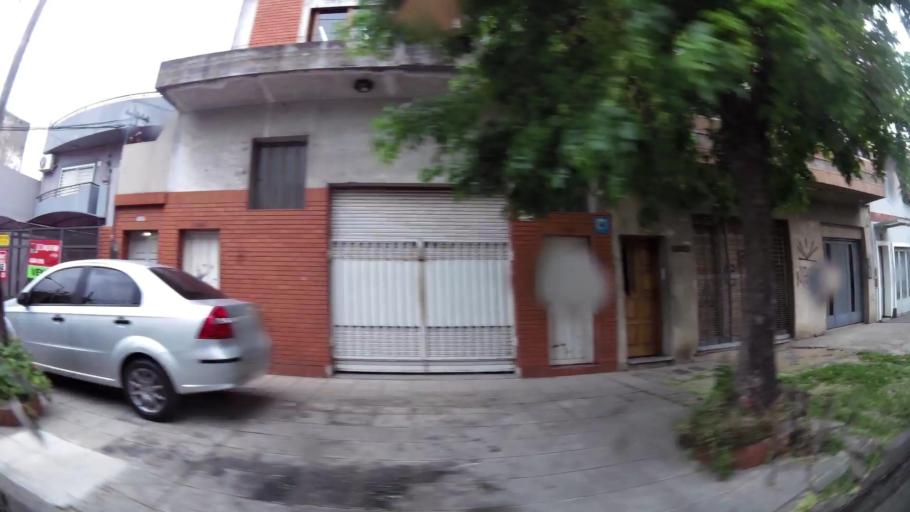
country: AR
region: Buenos Aires
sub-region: Partido de Lanus
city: Lanus
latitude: -34.6957
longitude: -58.4018
